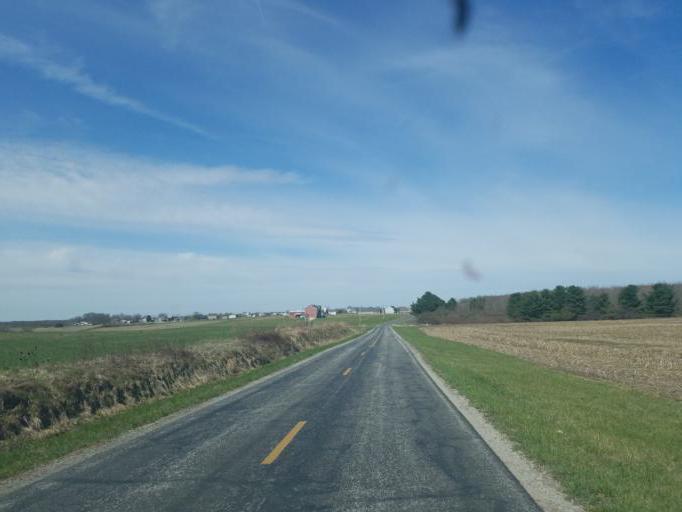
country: US
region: Ohio
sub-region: Delaware County
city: Delaware
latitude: 40.3495
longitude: -83.0432
